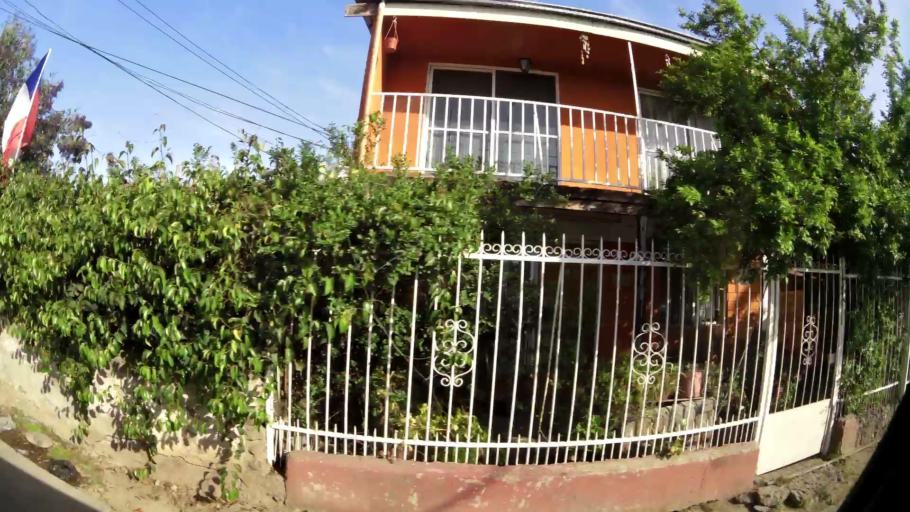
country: CL
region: Santiago Metropolitan
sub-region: Provincia de Santiago
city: Santiago
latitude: -33.5106
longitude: -70.6283
